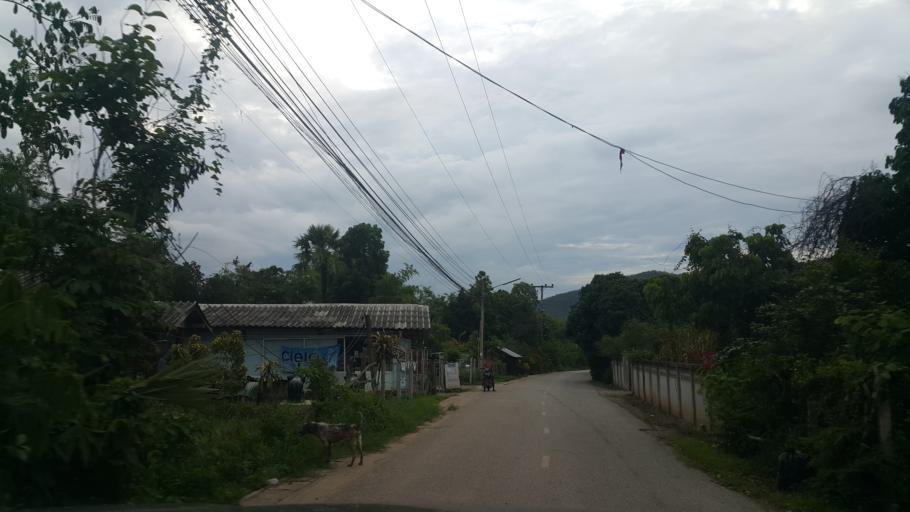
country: TH
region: Chiang Mai
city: Mae On
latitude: 18.7345
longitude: 99.2221
